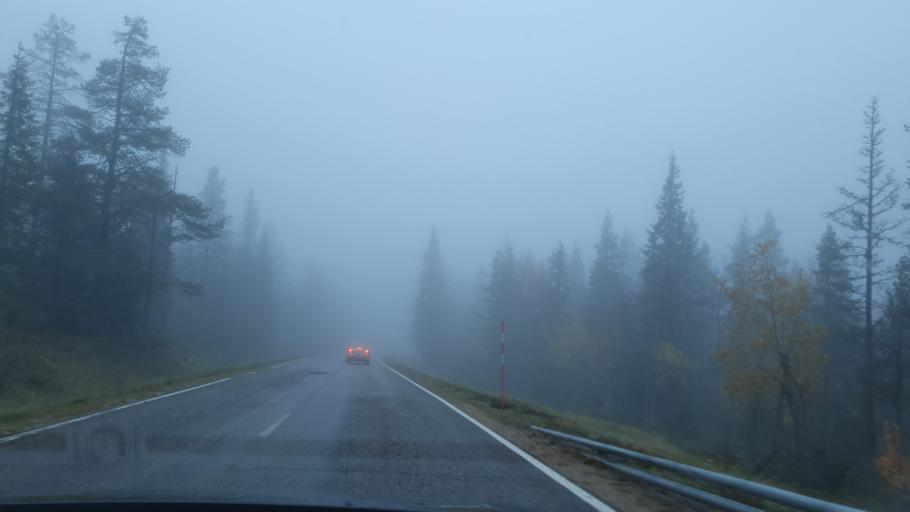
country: FI
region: Lapland
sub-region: Tunturi-Lappi
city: Kolari
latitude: 67.5415
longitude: 24.2146
